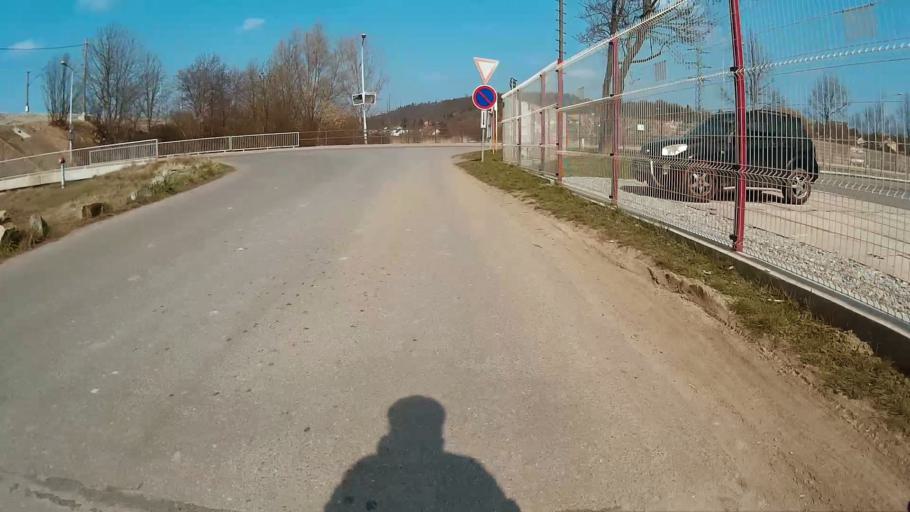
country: CZ
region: South Moravian
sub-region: Mesto Brno
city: Mokra Hora
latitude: 49.2562
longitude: 16.5911
